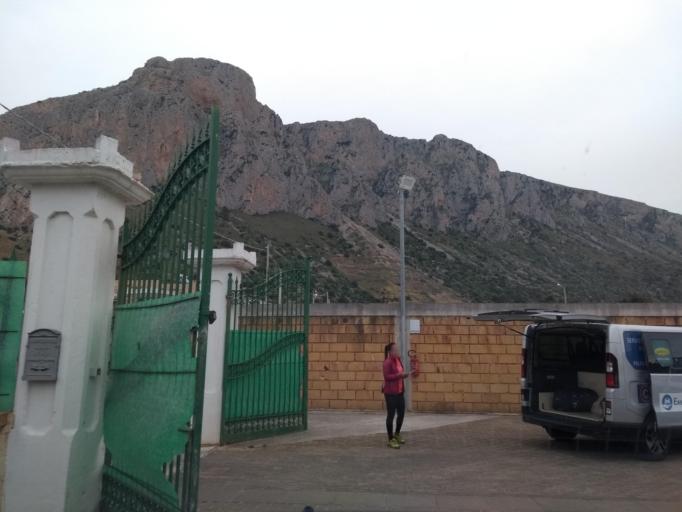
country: IT
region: Sicily
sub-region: Palermo
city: Cinisi
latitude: 38.1688
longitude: 13.1074
